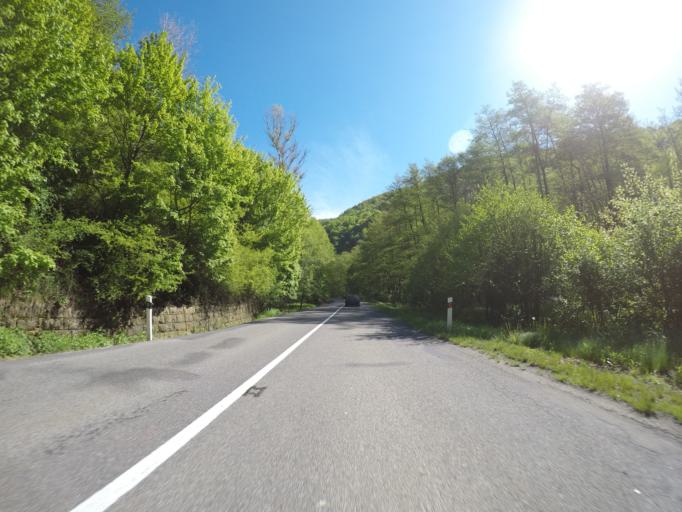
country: SK
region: Banskobystricky
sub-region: Okres Banska Bystrica
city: Banska Stiavnica
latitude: 48.5281
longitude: 19.0053
